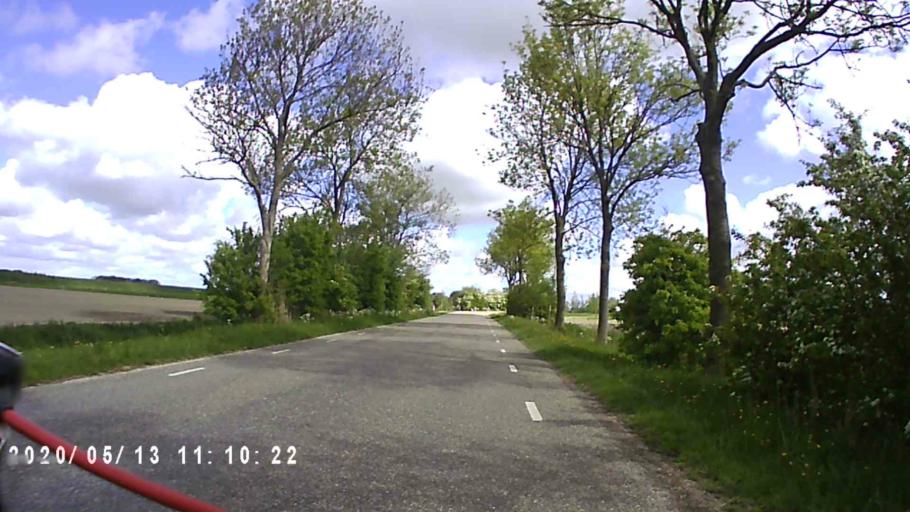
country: NL
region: Groningen
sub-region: Gemeente Zuidhorn
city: Oldehove
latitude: 53.2964
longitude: 6.3460
